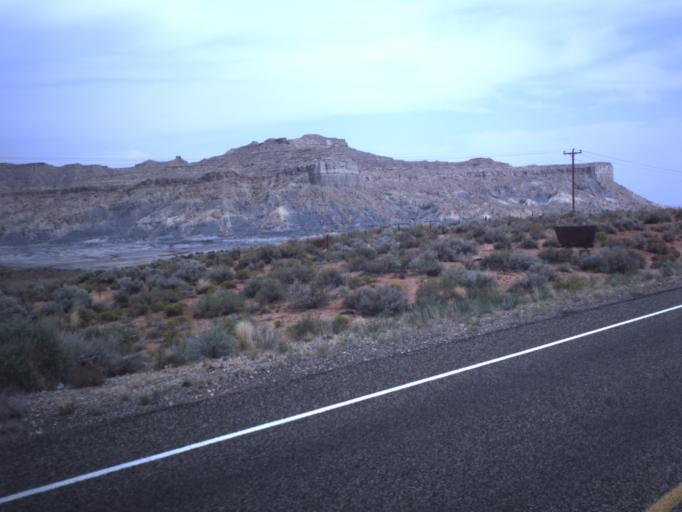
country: US
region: Arizona
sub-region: Coconino County
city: Page
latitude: 37.0755
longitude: -111.6575
